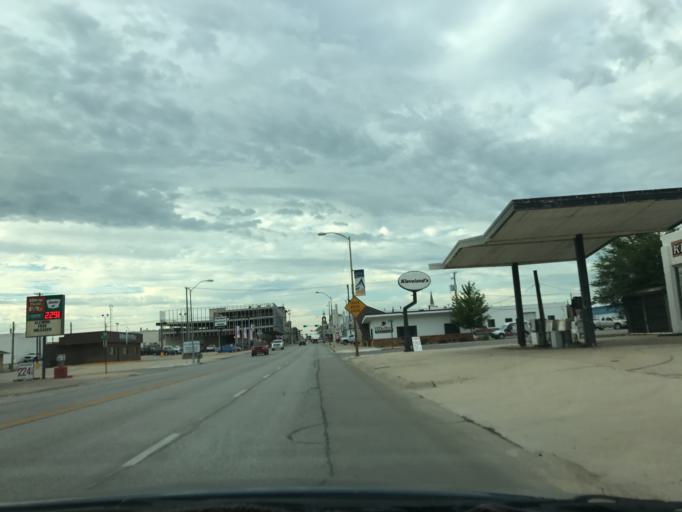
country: US
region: Nebraska
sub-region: Gage County
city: Beatrice
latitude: 40.2632
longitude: -96.7467
